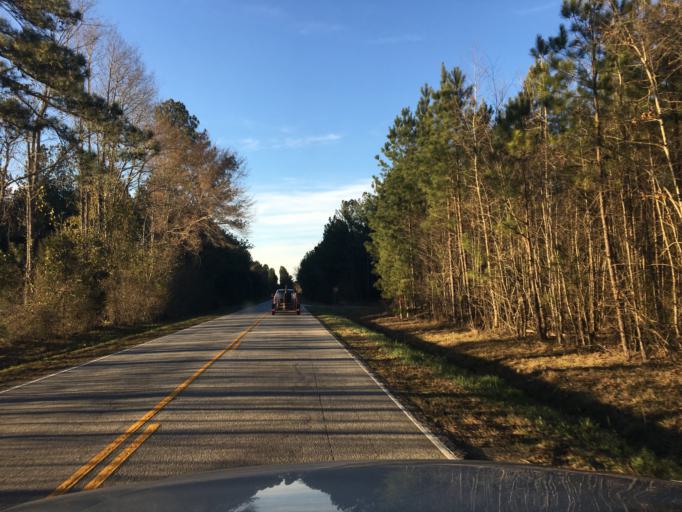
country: US
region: South Carolina
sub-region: Saluda County
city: Saluda
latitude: 34.1542
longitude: -81.8497
